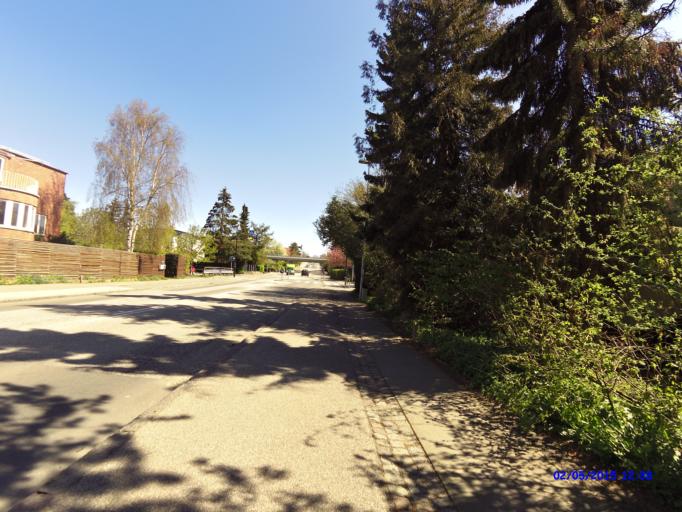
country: DK
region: Capital Region
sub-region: Lyngby-Tarbaek Kommune
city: Kongens Lyngby
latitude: 55.7316
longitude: 12.5340
